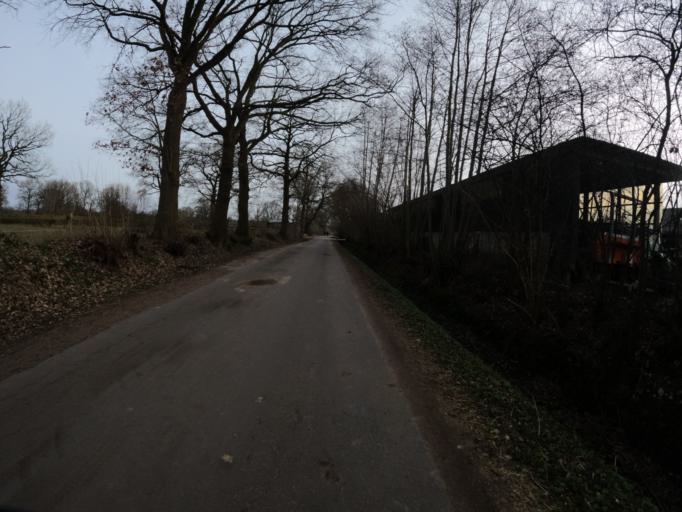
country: DE
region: Schleswig-Holstein
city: Rellingen
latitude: 53.5900
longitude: 9.7964
